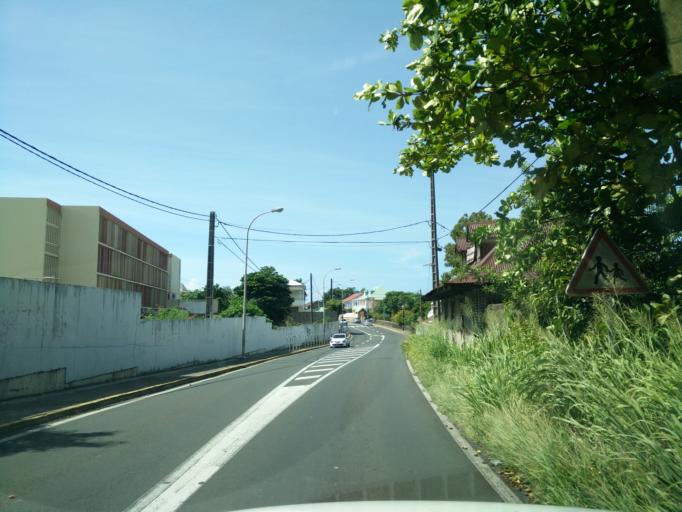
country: GP
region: Guadeloupe
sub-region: Guadeloupe
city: Basse-Terre
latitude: 15.9967
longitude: -61.7230
